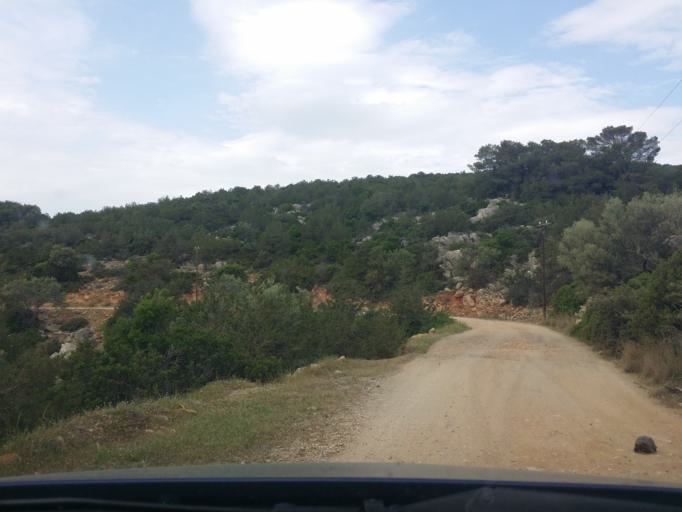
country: GR
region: Attica
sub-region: Nomos Piraios
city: Poros
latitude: 37.5385
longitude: 23.4825
